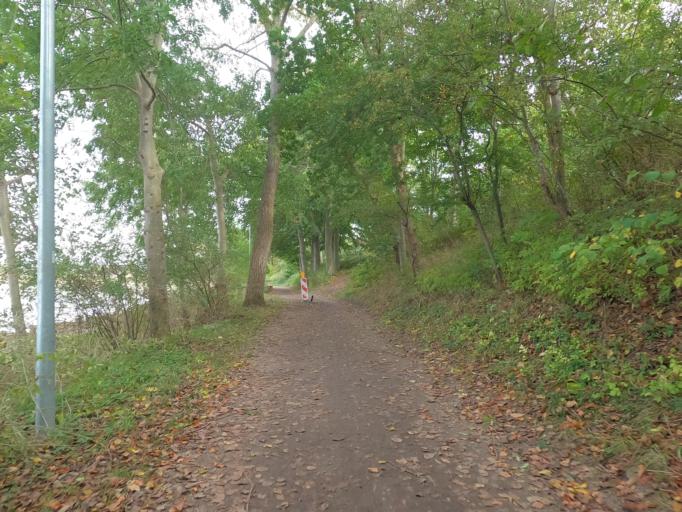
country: DE
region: Schleswig-Holstein
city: Heiligenhafen
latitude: 54.3695
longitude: 10.9977
